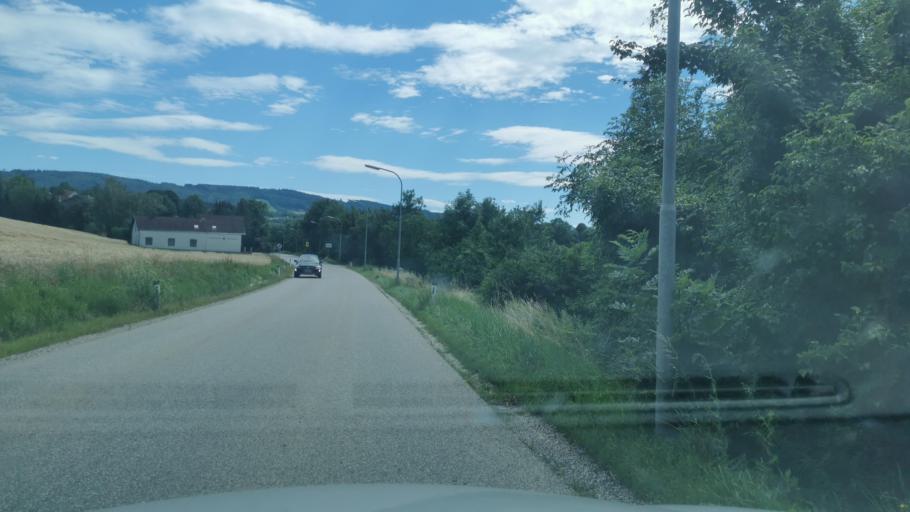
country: AT
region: Lower Austria
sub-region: Politischer Bezirk Sankt Polten
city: Pyhra
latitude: 48.1478
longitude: 15.6402
